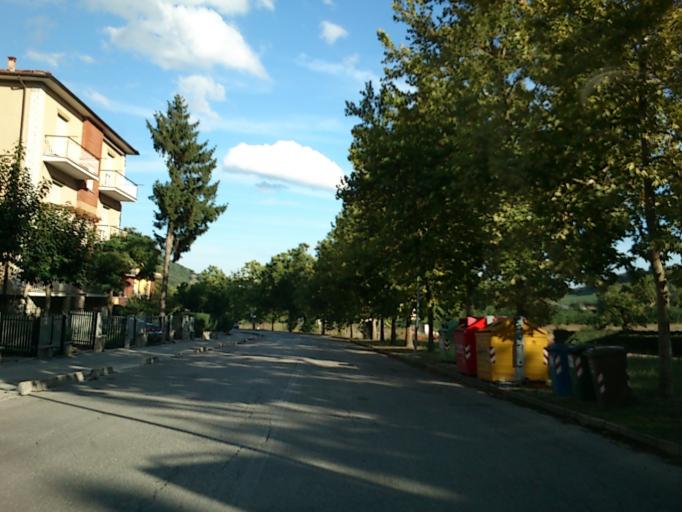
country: IT
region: The Marches
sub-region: Provincia di Pesaro e Urbino
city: Urbania
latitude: 43.6653
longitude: 12.5193
